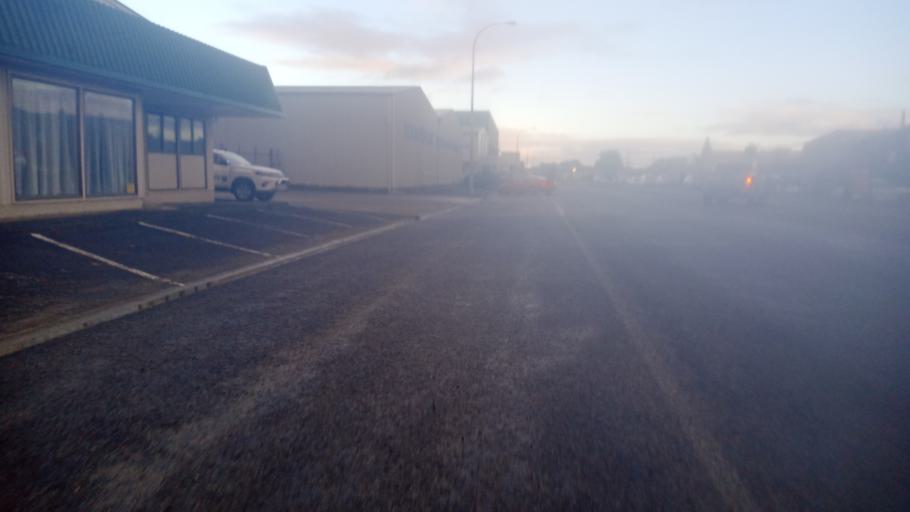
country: NZ
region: Gisborne
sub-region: Gisborne District
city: Gisborne
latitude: -38.6666
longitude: 177.9965
